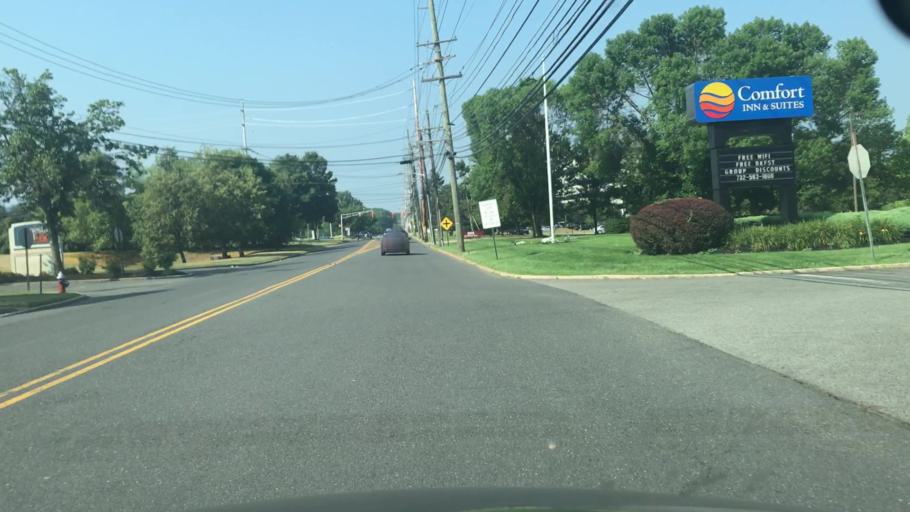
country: US
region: New Jersey
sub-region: Somerset County
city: South Bound Brook
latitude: 40.5349
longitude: -74.5262
